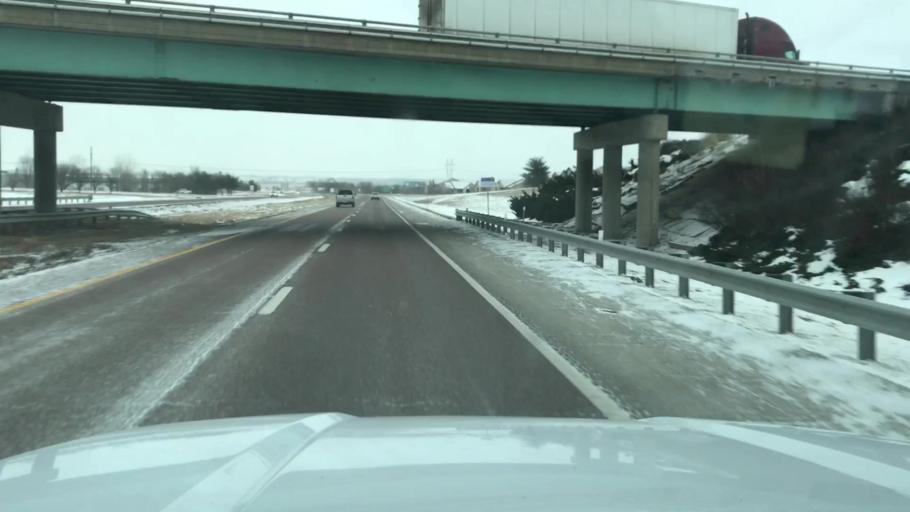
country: US
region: Missouri
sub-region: Buchanan County
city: Saint Joseph
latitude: 39.7495
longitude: -94.7683
